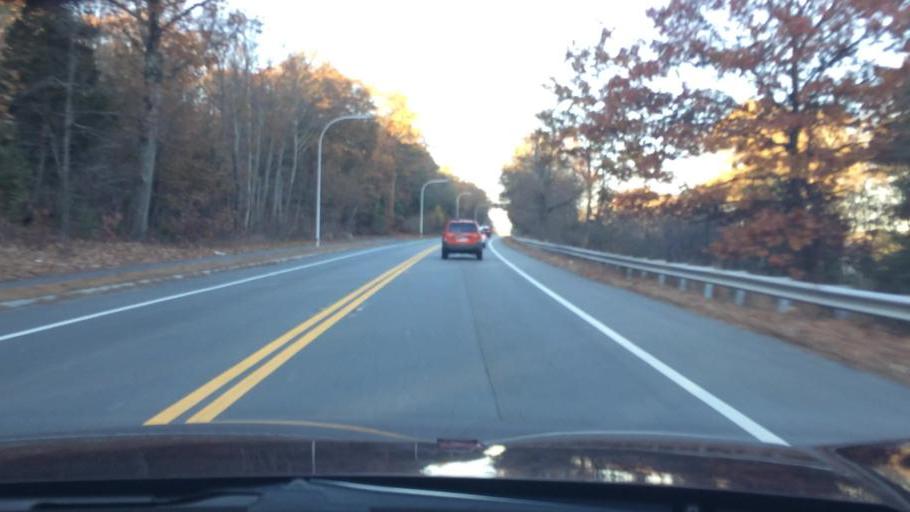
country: US
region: Massachusetts
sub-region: Norfolk County
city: Norwood
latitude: 42.2077
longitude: -71.1952
